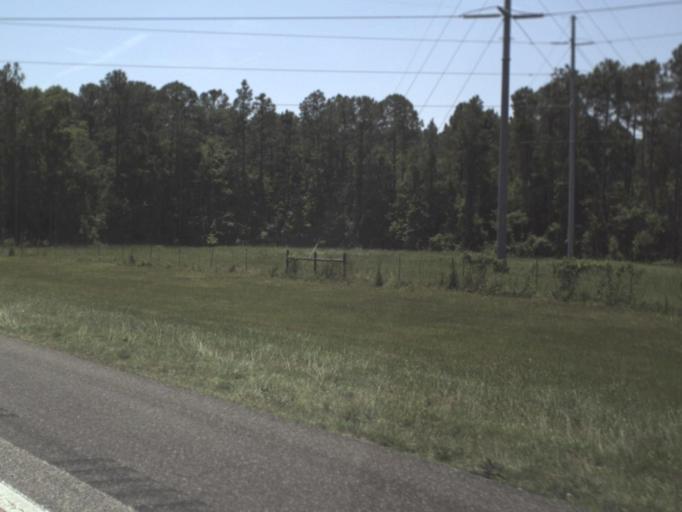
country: US
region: Florida
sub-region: Saint Johns County
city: Fruit Cove
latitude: 30.1484
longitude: -81.5456
